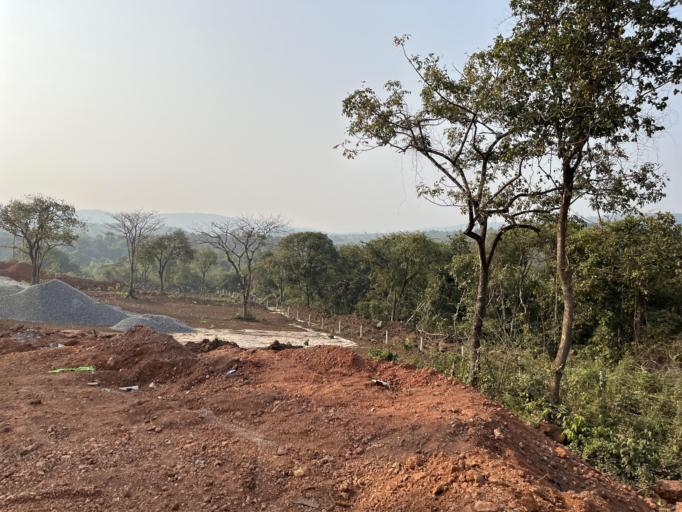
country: IN
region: Goa
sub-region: North Goa
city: Pernem
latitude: 15.6965
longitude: 73.8386
